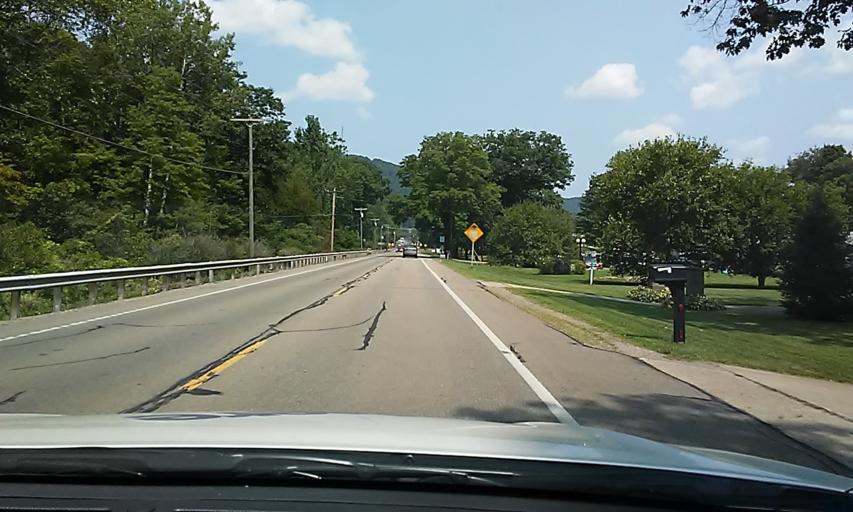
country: US
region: Pennsylvania
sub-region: Cameron County
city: Emporium
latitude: 41.5062
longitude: -78.2535
